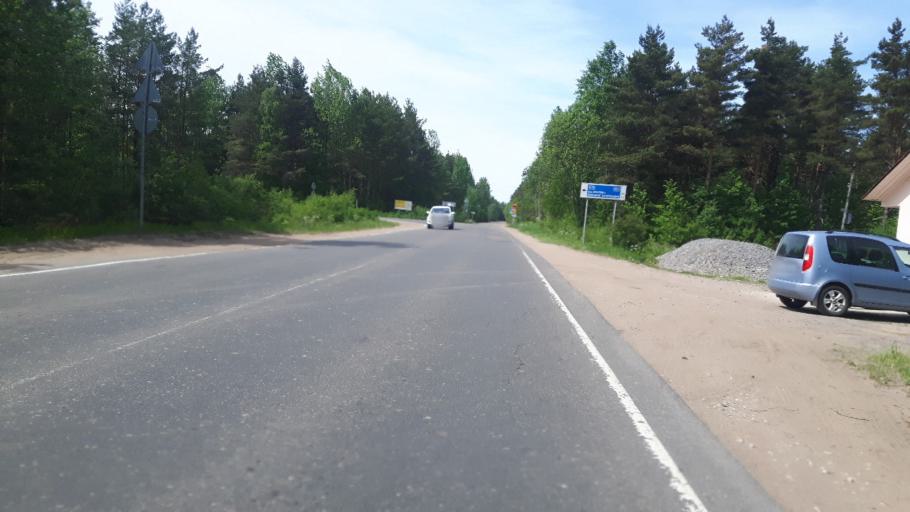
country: RU
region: Leningrad
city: Ust'-Luga
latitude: 59.6576
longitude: 28.2506
